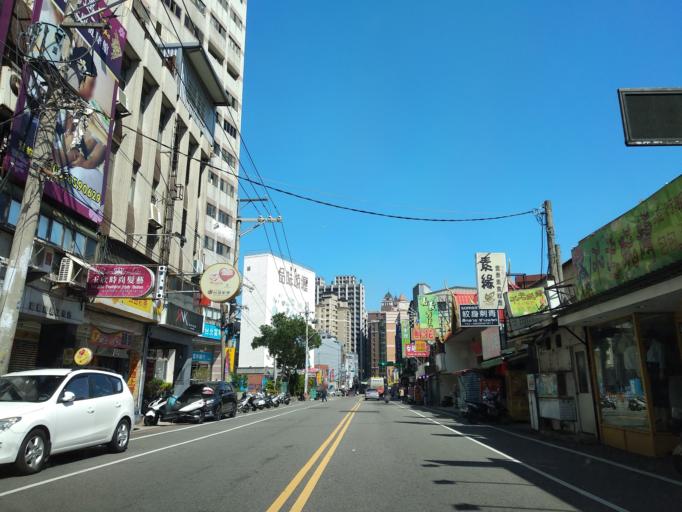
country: TW
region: Taiwan
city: Taoyuan City
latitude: 24.9513
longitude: 121.2258
